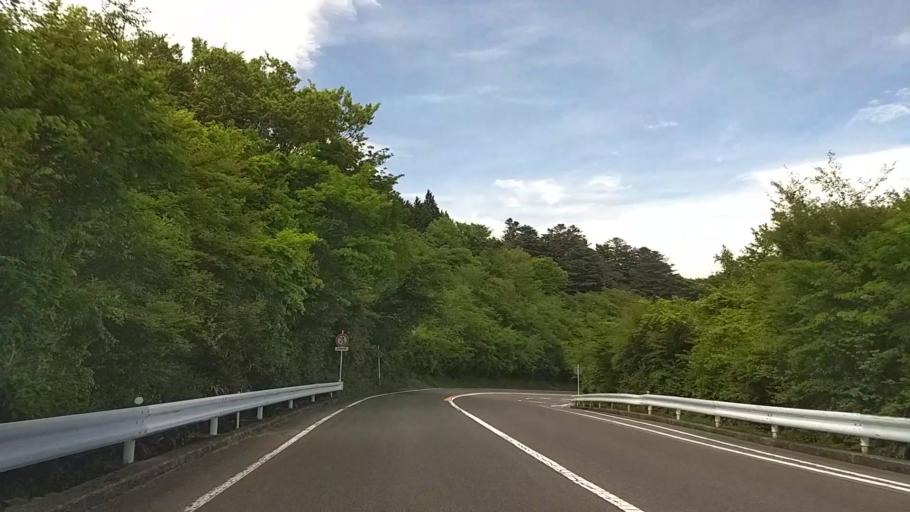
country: JP
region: Kanagawa
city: Yugawara
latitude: 35.2044
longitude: 139.0887
